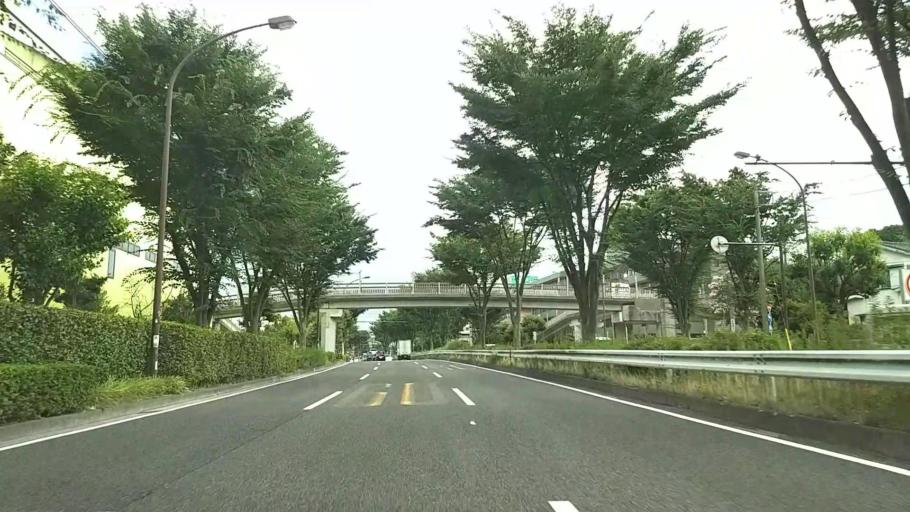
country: JP
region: Kanagawa
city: Yokohama
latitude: 35.4123
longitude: 139.5602
